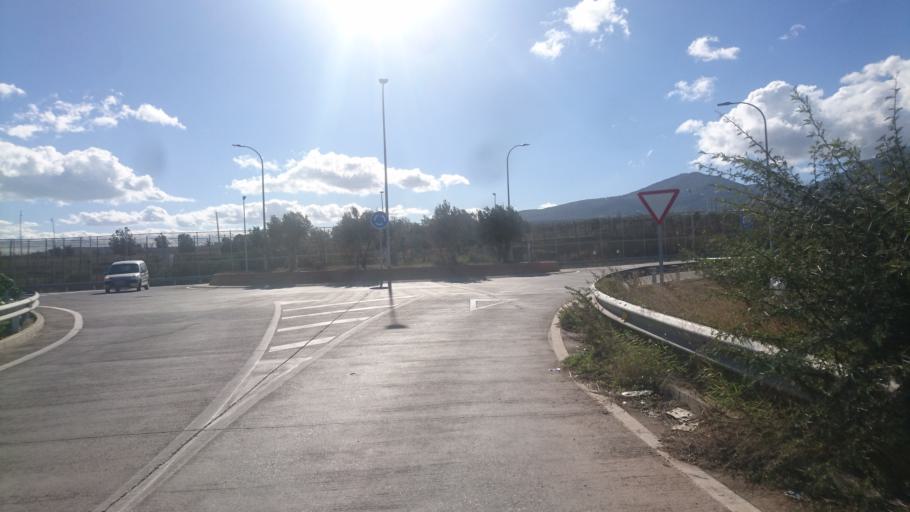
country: ES
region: Melilla
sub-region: Melilla
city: Melilla
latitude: 35.2679
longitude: -2.9405
